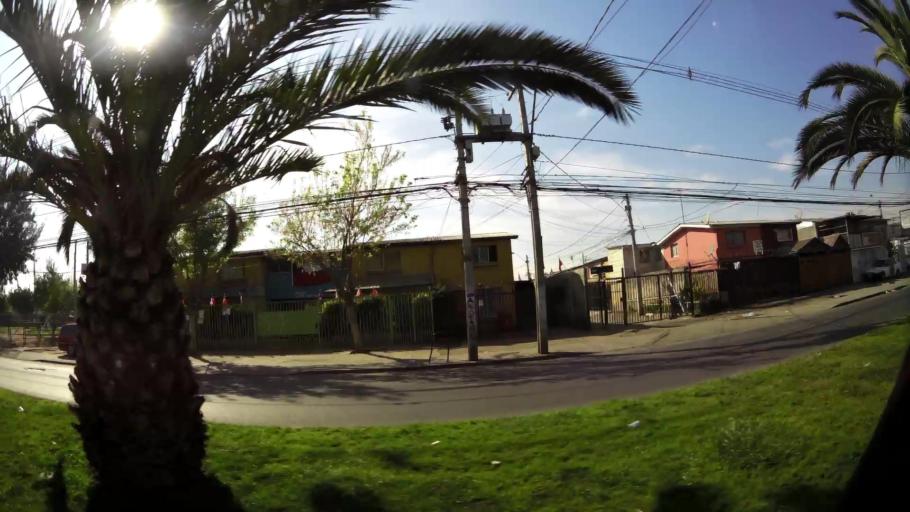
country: CL
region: Santiago Metropolitan
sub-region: Provincia de Santiago
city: Lo Prado
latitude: -33.4594
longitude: -70.7520
